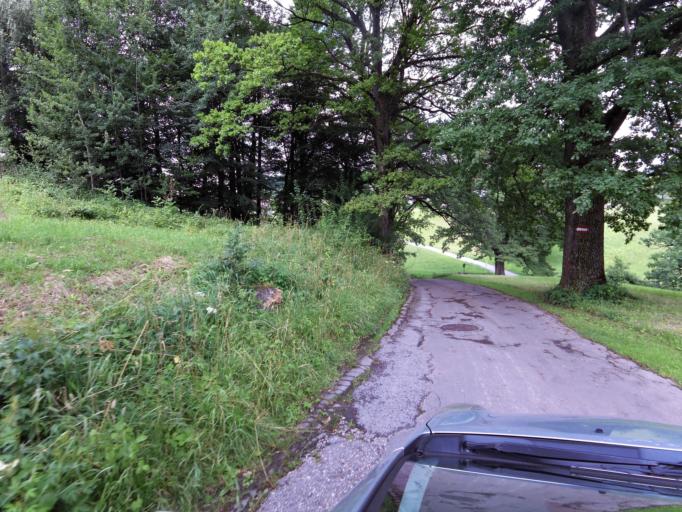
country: AT
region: Salzburg
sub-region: Politischer Bezirk Salzburg-Umgebung
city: Hallwang
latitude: 47.8178
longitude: 13.0817
